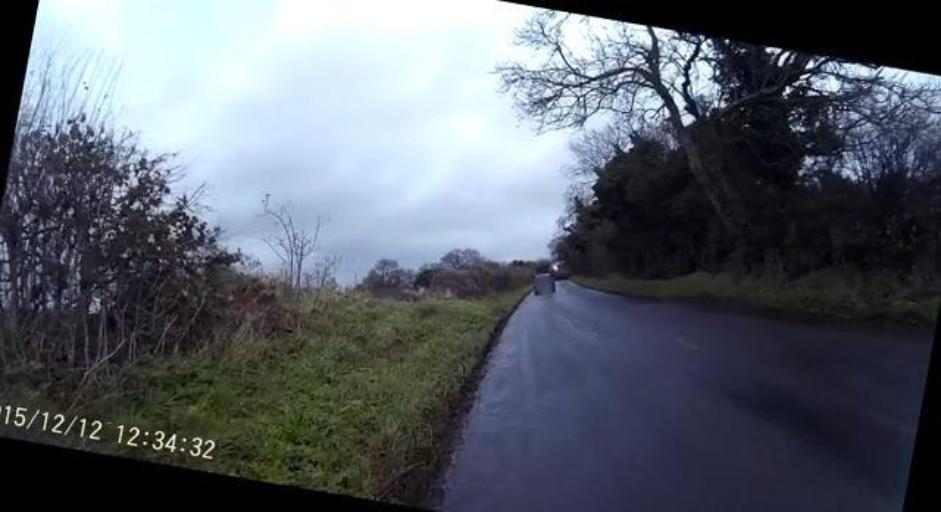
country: GB
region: England
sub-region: Hampshire
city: Cowplain
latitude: 50.9522
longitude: -0.9881
